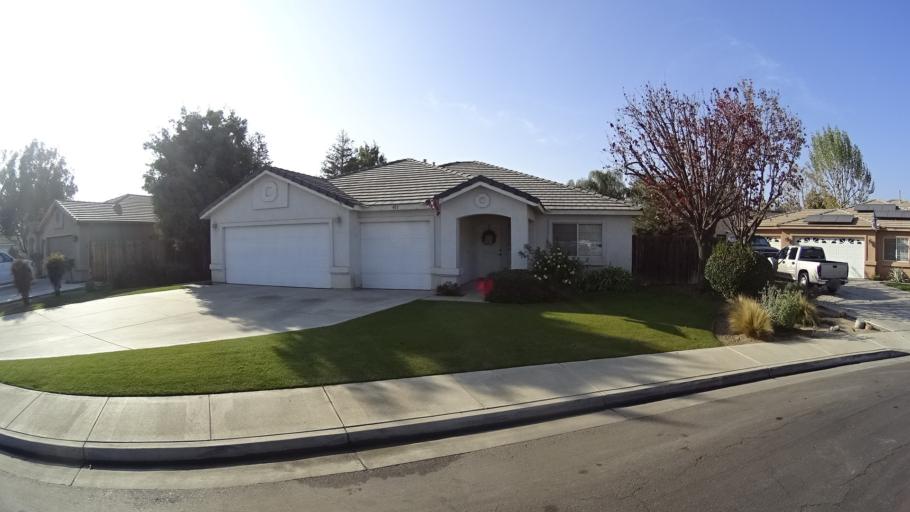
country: US
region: California
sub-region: Kern County
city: Rosedale
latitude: 35.3588
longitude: -119.1596
